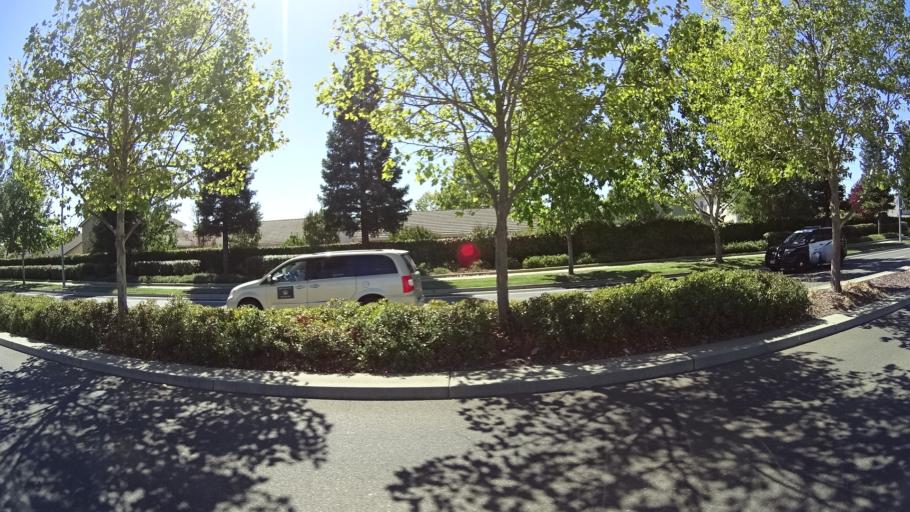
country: US
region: California
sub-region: Sacramento County
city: Elk Grove
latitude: 38.4237
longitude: -121.3409
